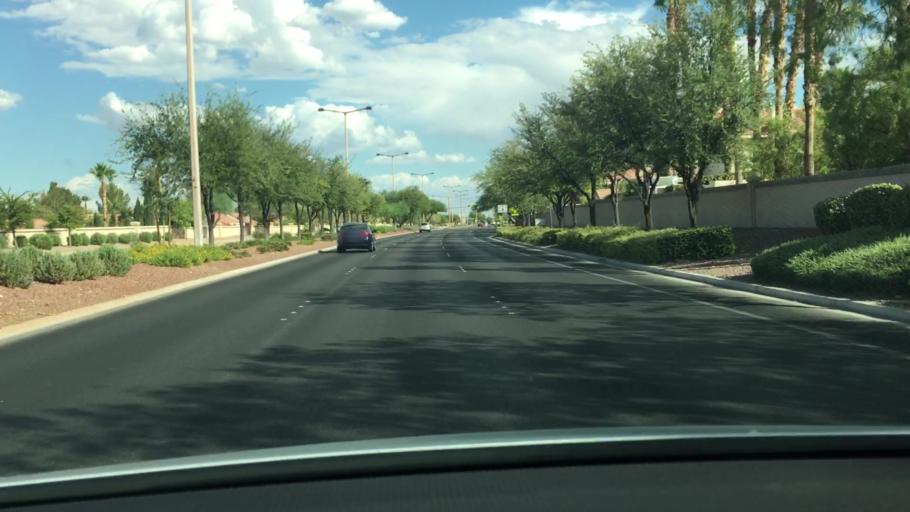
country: US
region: Nevada
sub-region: Clark County
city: Summerlin South
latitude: 36.2033
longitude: -115.2882
